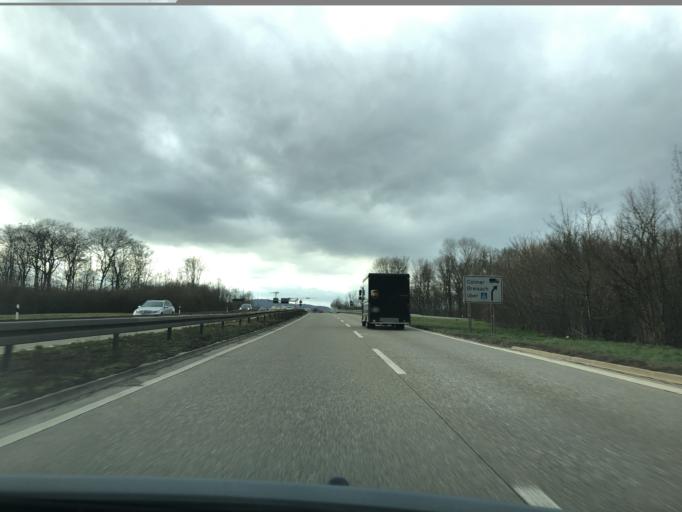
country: DE
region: Baden-Wuerttemberg
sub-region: Freiburg Region
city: Umkirch
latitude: 48.0220
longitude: 7.7869
